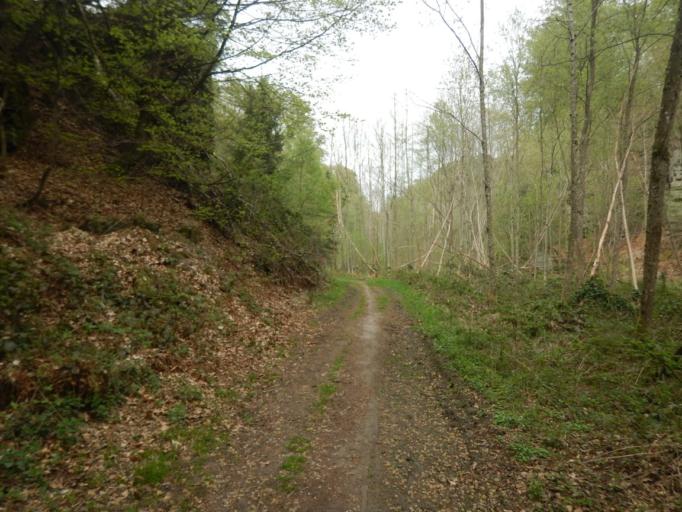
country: LU
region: Grevenmacher
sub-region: Canton d'Echternach
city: Consdorf
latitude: 49.7676
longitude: 6.3446
